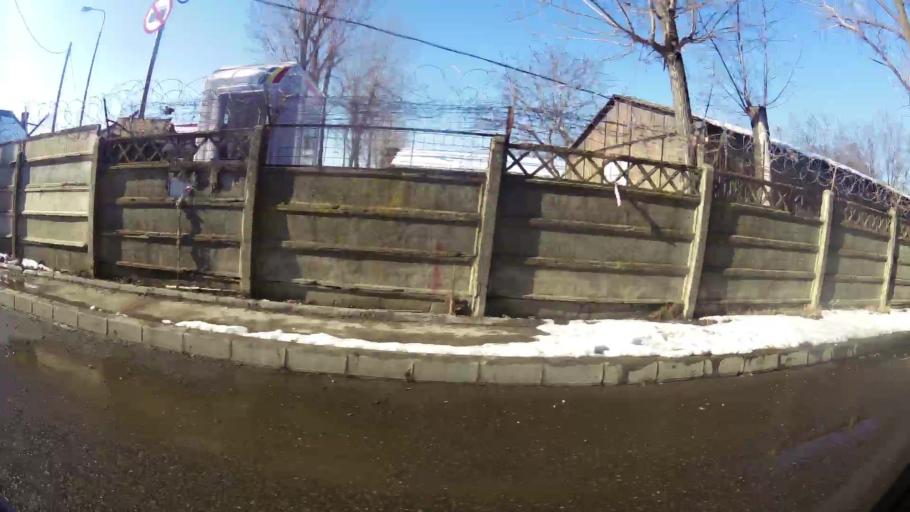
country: RO
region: Ilfov
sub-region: Comuna Magurele
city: Magurele
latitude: 44.3884
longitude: 26.0531
